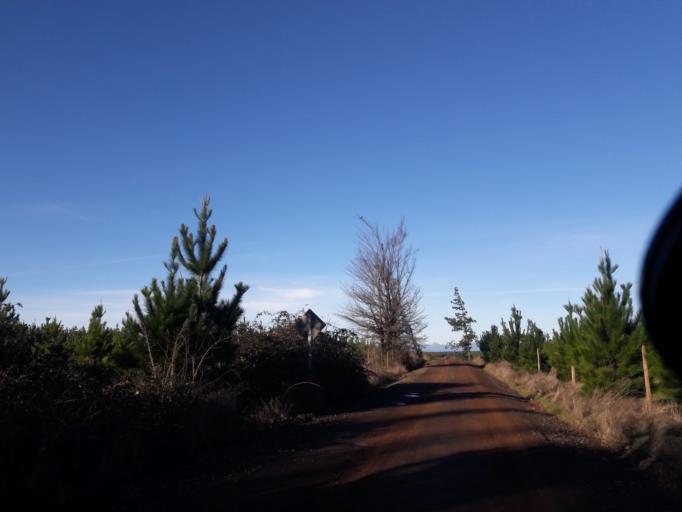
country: CL
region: Biobio
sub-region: Provincia de Biobio
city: Cabrero
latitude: -37.0098
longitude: -72.1811
